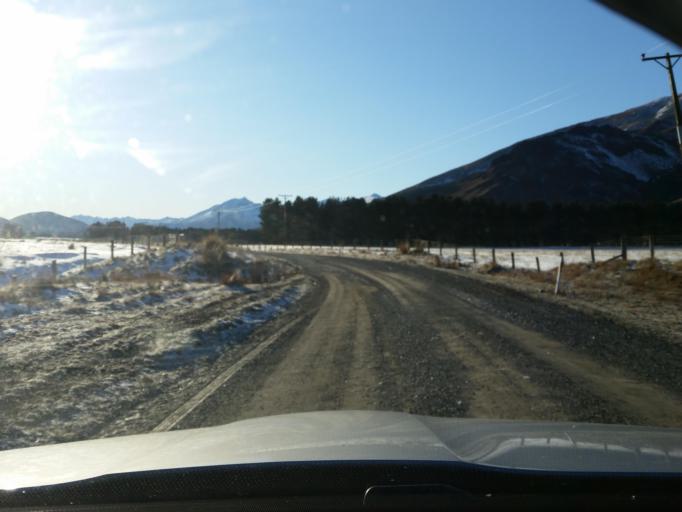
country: NZ
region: Southland
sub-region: Southland District
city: Te Anau
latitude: -45.3635
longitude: 168.1116
